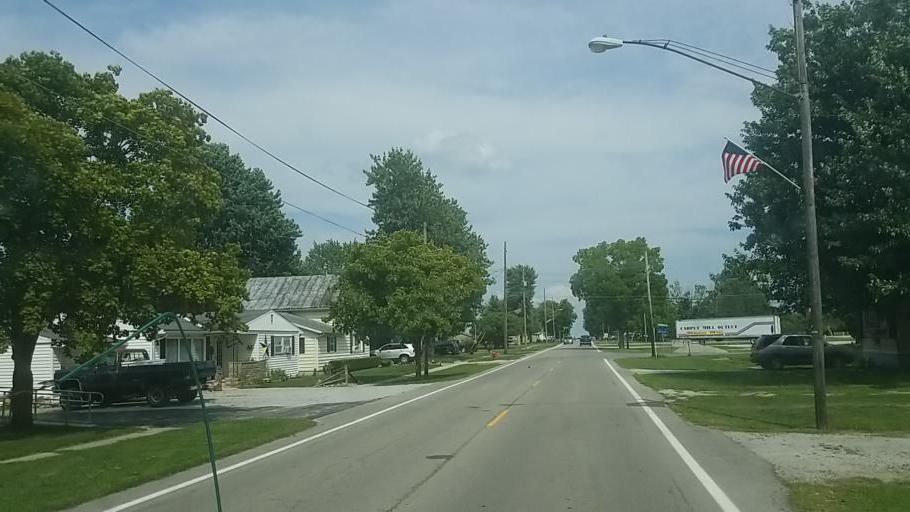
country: US
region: Ohio
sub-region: Hardin County
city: Forest
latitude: 40.8017
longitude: -83.5059
